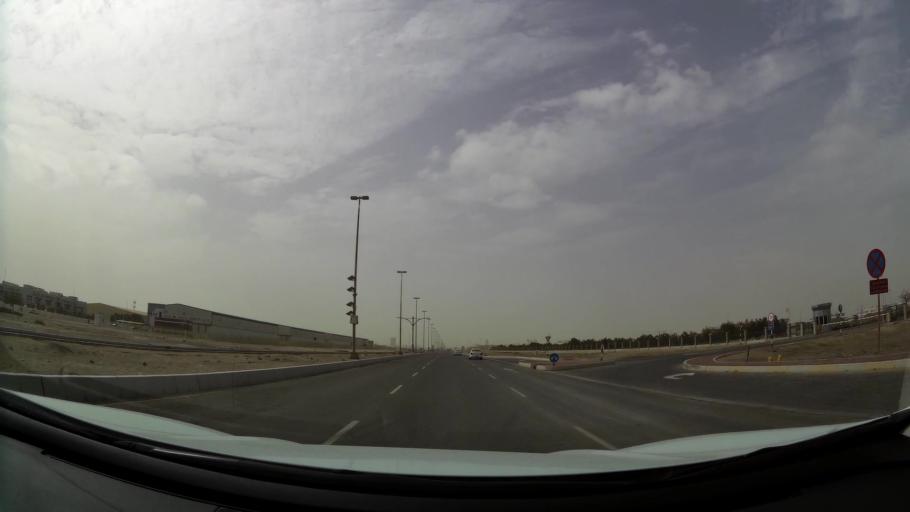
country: AE
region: Abu Dhabi
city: Abu Dhabi
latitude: 24.3376
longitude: 54.5225
